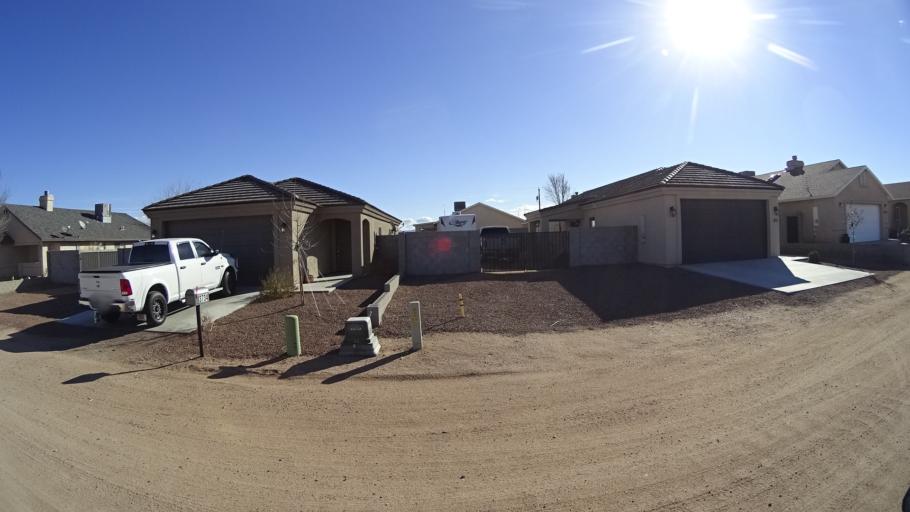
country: US
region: Arizona
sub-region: Mohave County
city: New Kingman-Butler
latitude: 35.2318
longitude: -114.0132
